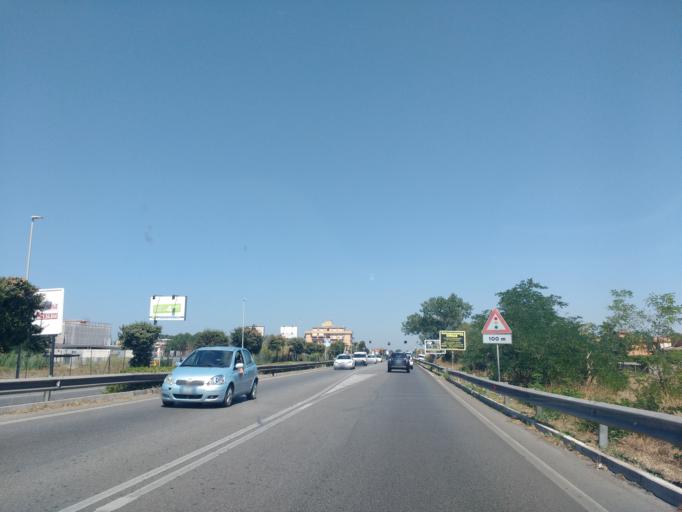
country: IT
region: Latium
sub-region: Citta metropolitana di Roma Capitale
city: Lido di Ostia
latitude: 41.7609
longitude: 12.2688
